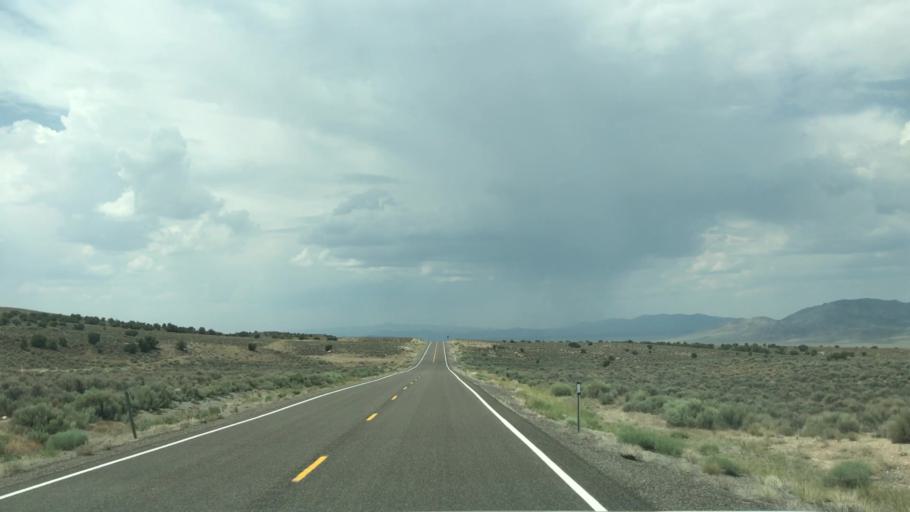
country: US
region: Nevada
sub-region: Eureka County
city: Eureka
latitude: 39.3973
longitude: -115.7147
